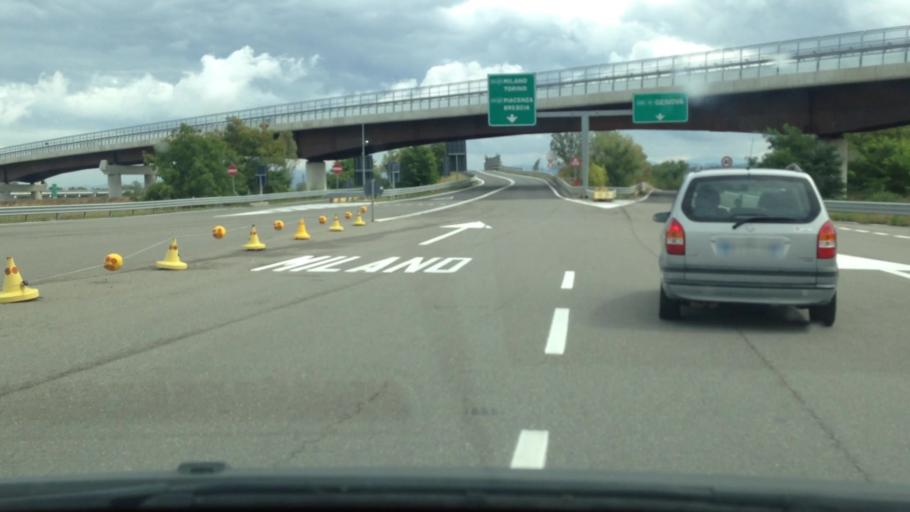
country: IT
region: Piedmont
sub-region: Provincia di Alessandria
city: Tortona
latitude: 44.9089
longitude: 8.8401
